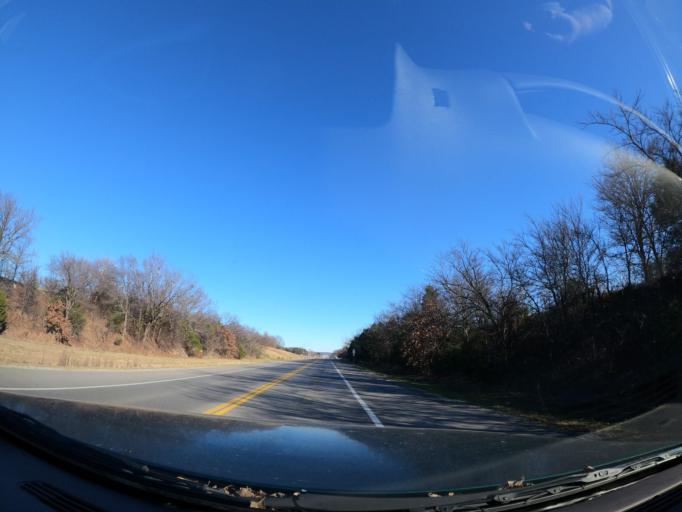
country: US
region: Oklahoma
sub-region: Pittsburg County
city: Longtown
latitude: 35.2392
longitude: -95.5422
